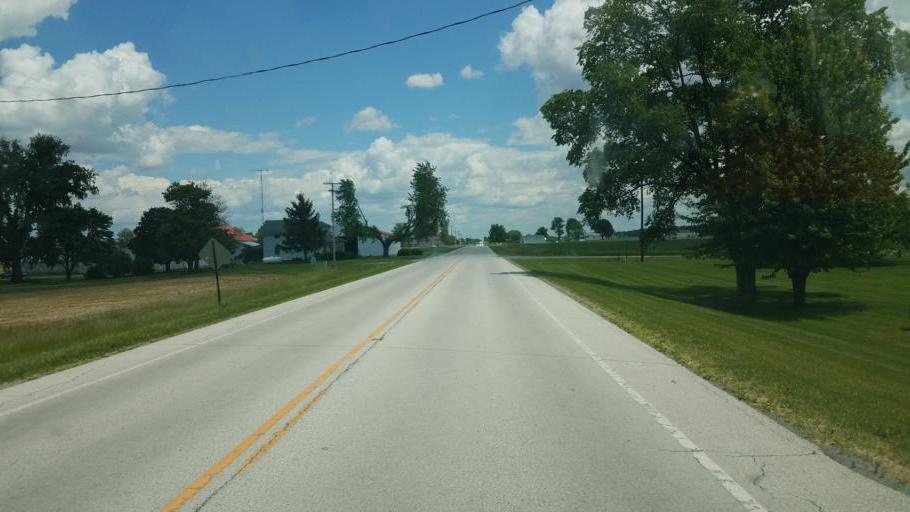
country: US
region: Ohio
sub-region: Wyandot County
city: Upper Sandusky
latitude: 40.8405
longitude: -83.1901
